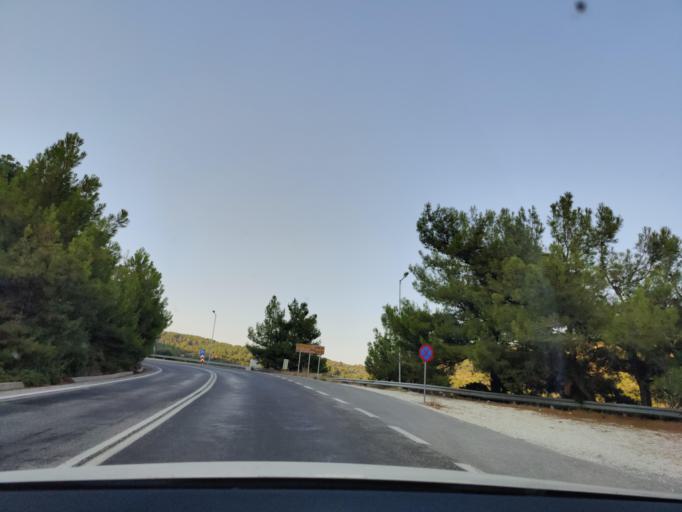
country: GR
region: East Macedonia and Thrace
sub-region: Nomos Kavalas
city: Potamia
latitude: 40.6173
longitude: 24.7581
